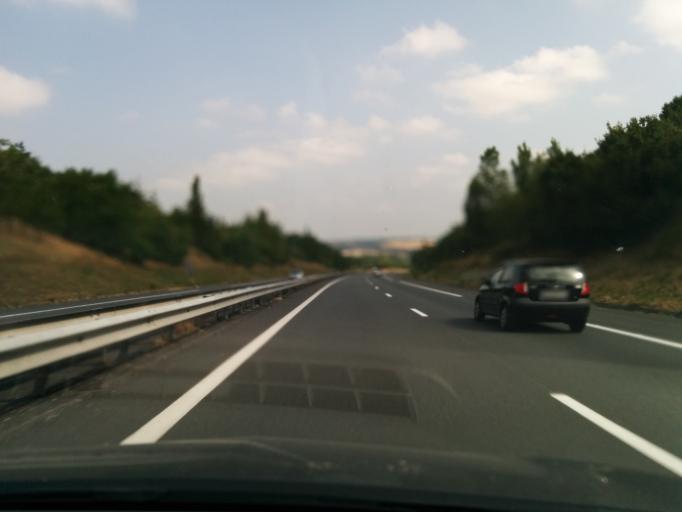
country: FR
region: Midi-Pyrenees
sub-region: Departement de la Haute-Garonne
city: Gragnague
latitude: 43.6794
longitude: 1.5610
